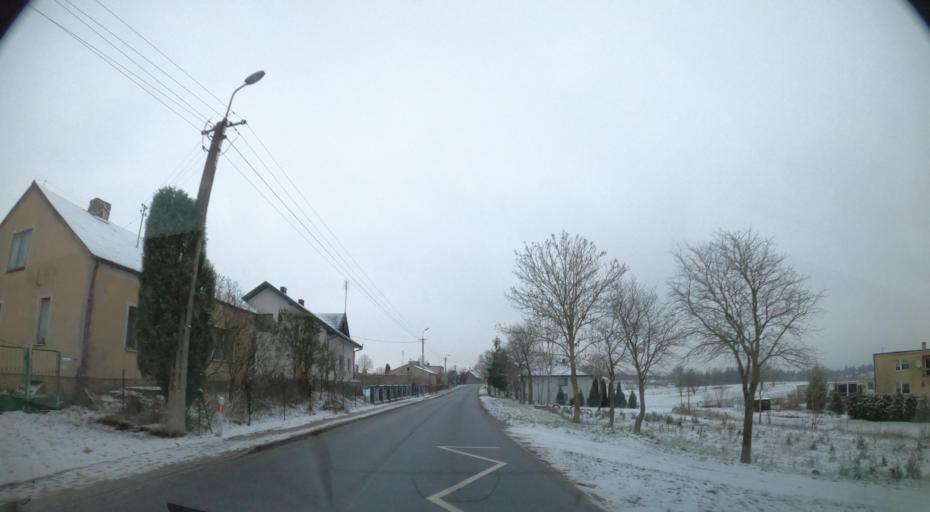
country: PL
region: Kujawsko-Pomorskie
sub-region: Powiat lipnowski
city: Wielgie
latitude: 52.6902
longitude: 19.2802
